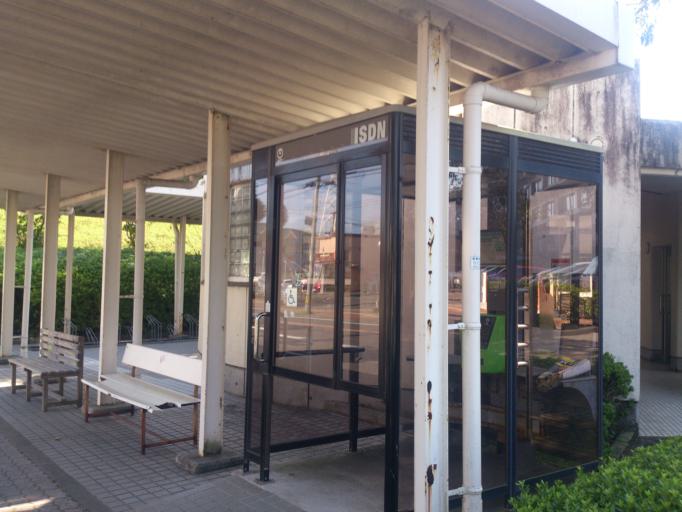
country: JP
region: Kagoshima
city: Kanoya
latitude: 31.3781
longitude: 130.8534
